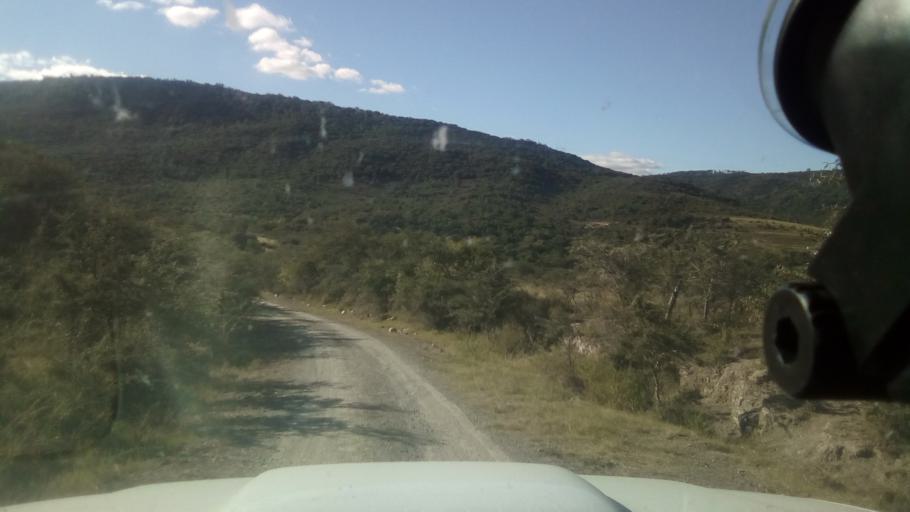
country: ZA
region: Eastern Cape
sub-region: Buffalo City Metropolitan Municipality
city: Bhisho
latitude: -32.7299
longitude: 27.3486
